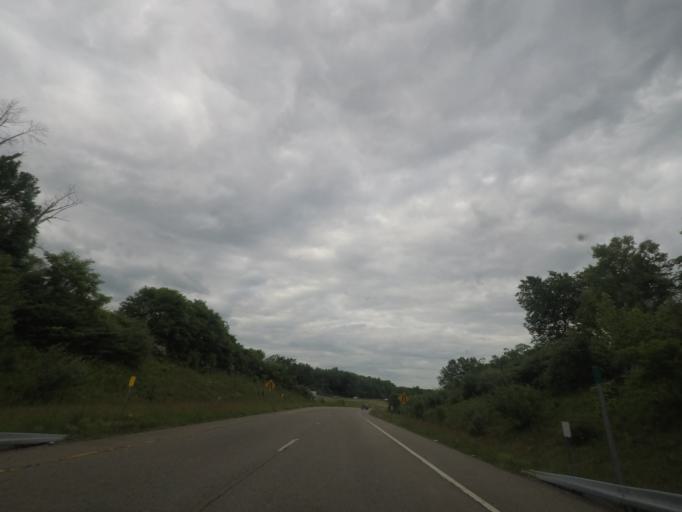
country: US
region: New York
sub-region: Orange County
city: Orange Lake
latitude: 41.5117
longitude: -74.1272
